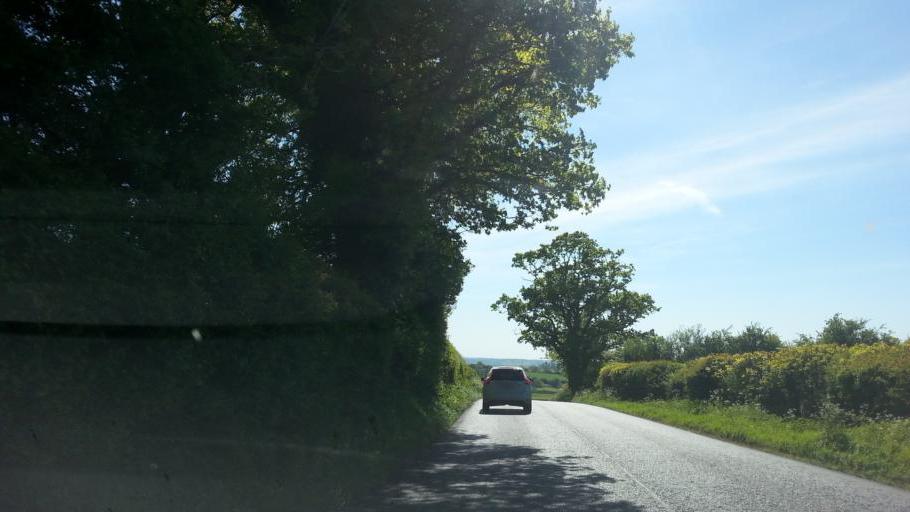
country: GB
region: England
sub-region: Dorset
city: Gillingham
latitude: 51.0077
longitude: -2.2652
